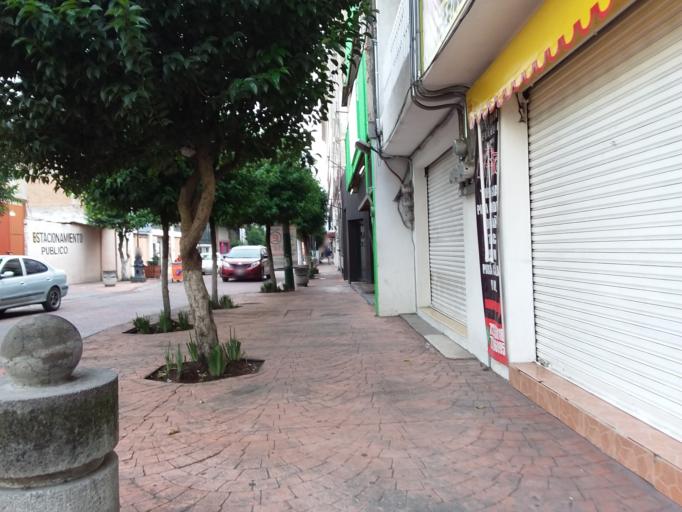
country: MX
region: Mexico
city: Toluca
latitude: 19.2890
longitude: -99.6558
